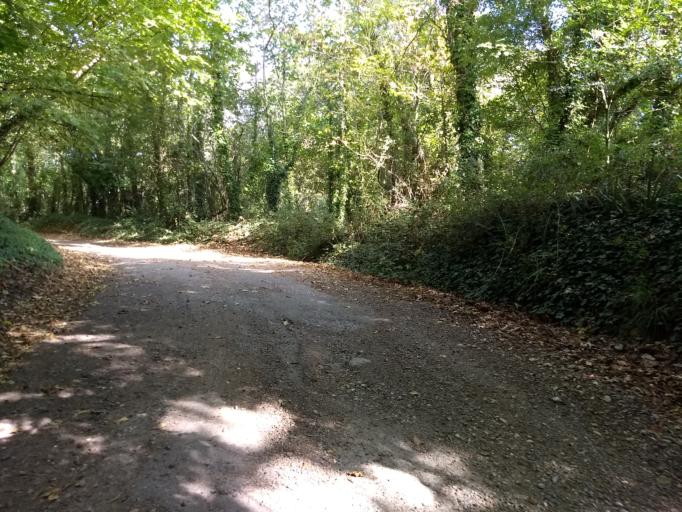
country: GB
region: England
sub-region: Isle of Wight
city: Brading
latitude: 50.7020
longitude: -1.1418
